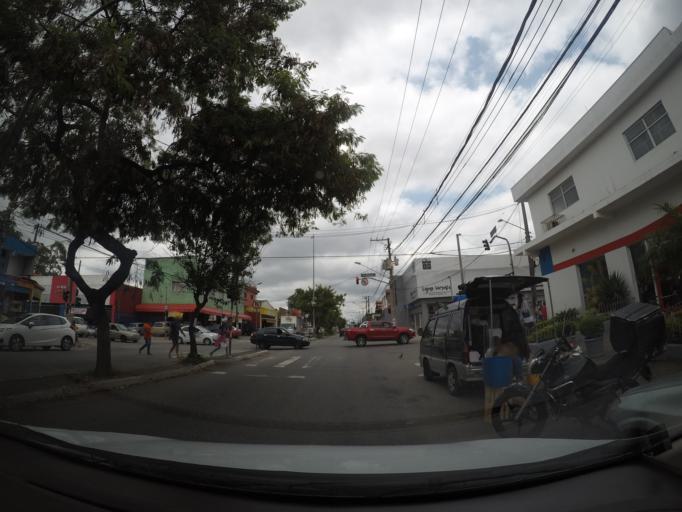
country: BR
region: Sao Paulo
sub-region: Itaquaquecetuba
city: Itaquaquecetuba
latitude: -23.4283
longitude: -46.4343
